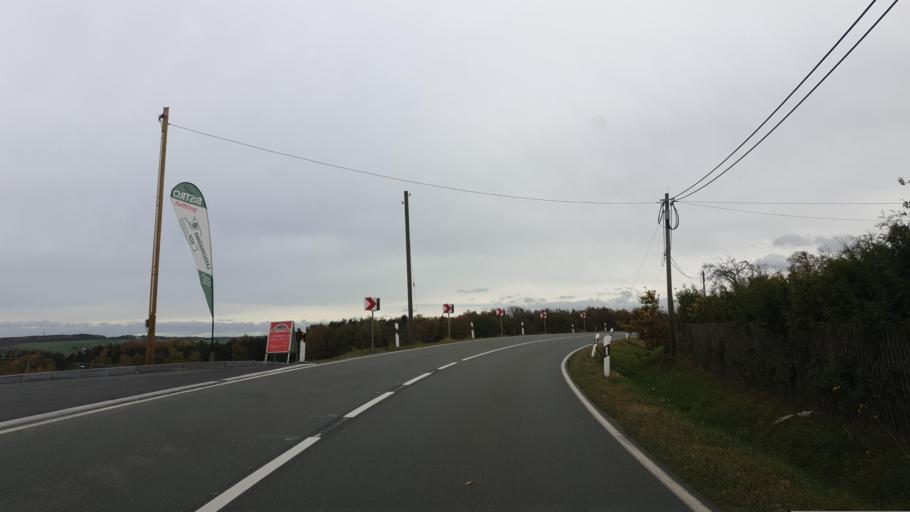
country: DE
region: Saxony
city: Limbach
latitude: 50.5924
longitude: 12.2718
